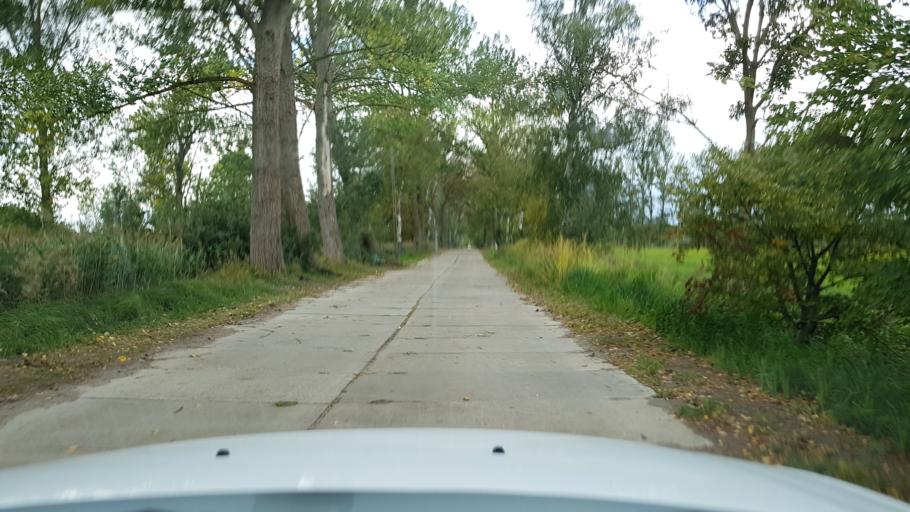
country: PL
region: West Pomeranian Voivodeship
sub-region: Powiat gryfinski
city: Gryfino
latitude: 53.3191
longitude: 14.5324
